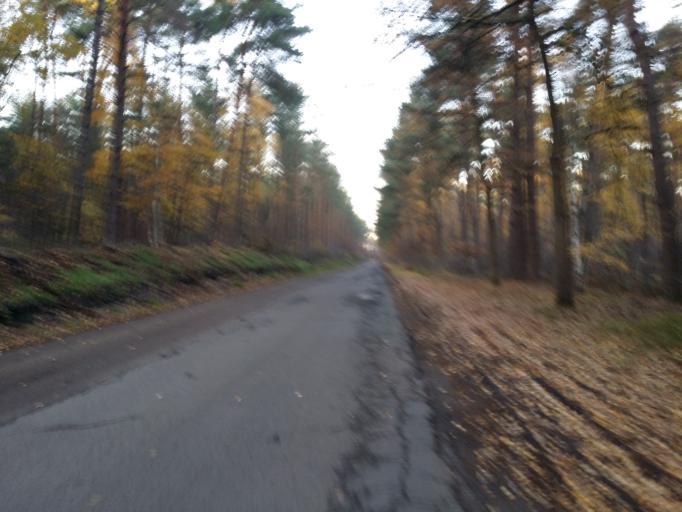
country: DE
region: Lower Saxony
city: Ahausen
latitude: 53.0787
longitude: 9.3059
